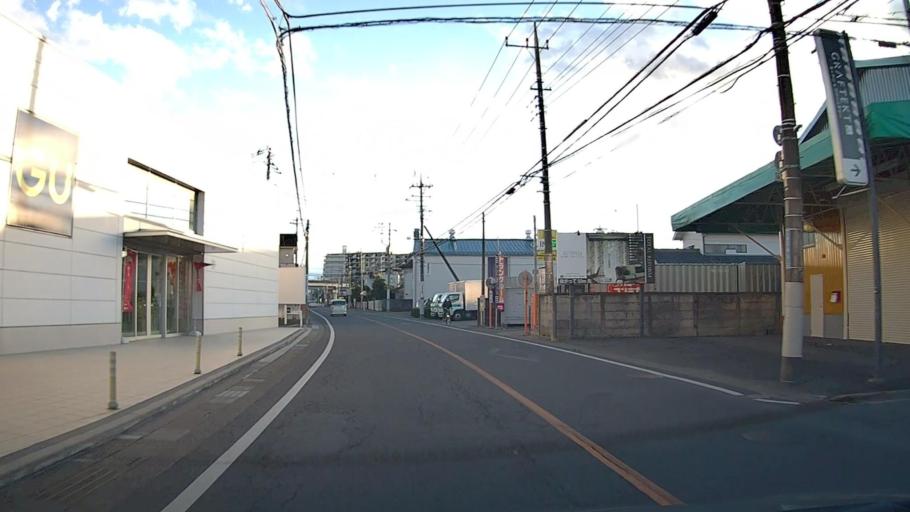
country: JP
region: Saitama
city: Shiki
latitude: 35.8103
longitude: 139.5762
